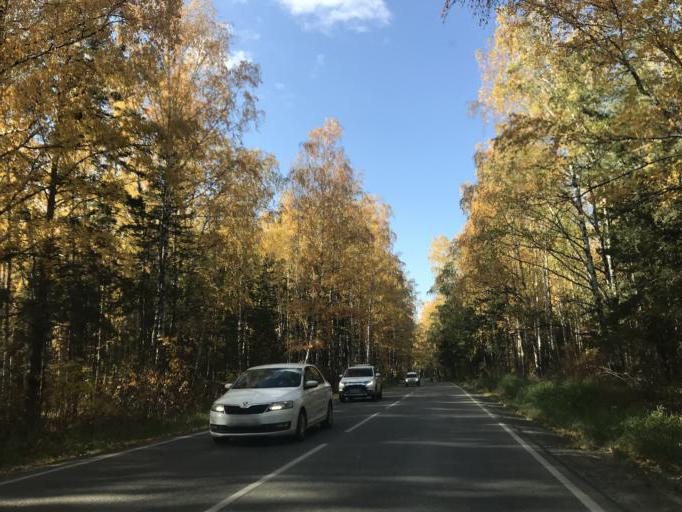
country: RU
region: Chelyabinsk
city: Dolgoderevenskoye
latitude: 55.2827
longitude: 61.3627
